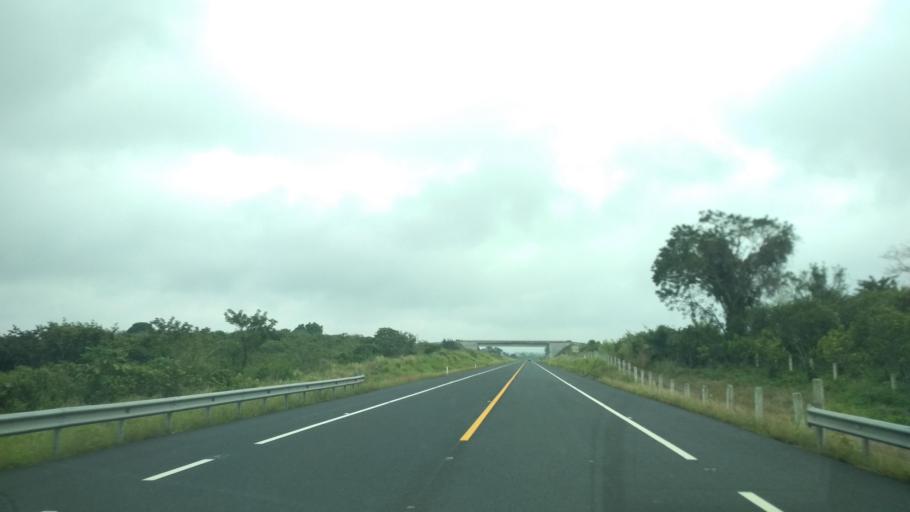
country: MX
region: Veracruz
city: Vega de San Marcos
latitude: 20.1925
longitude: -96.9714
